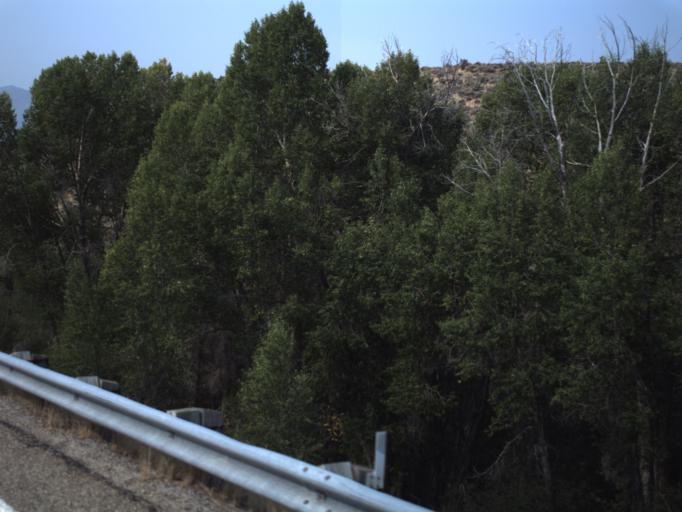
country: US
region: Utah
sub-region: Morgan County
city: Morgan
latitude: 40.9402
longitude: -111.5593
